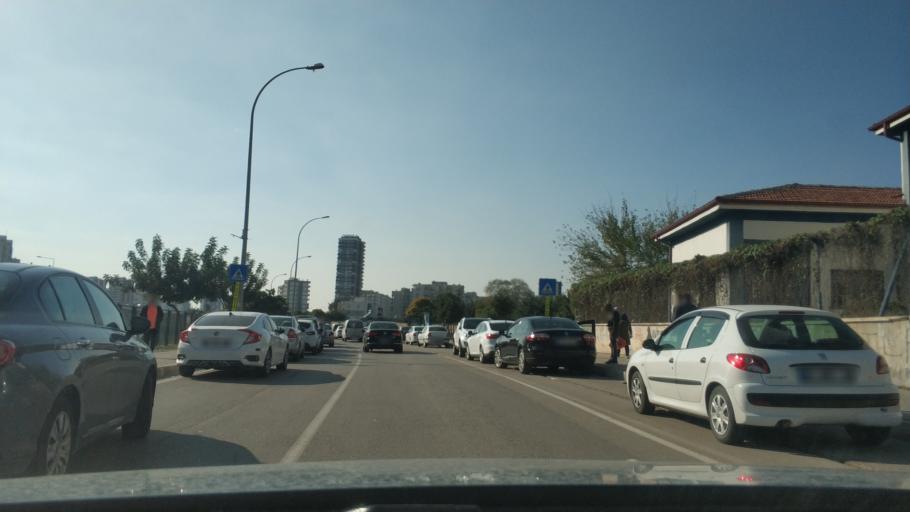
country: TR
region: Adana
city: Seyhan
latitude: 37.0120
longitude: 35.2774
